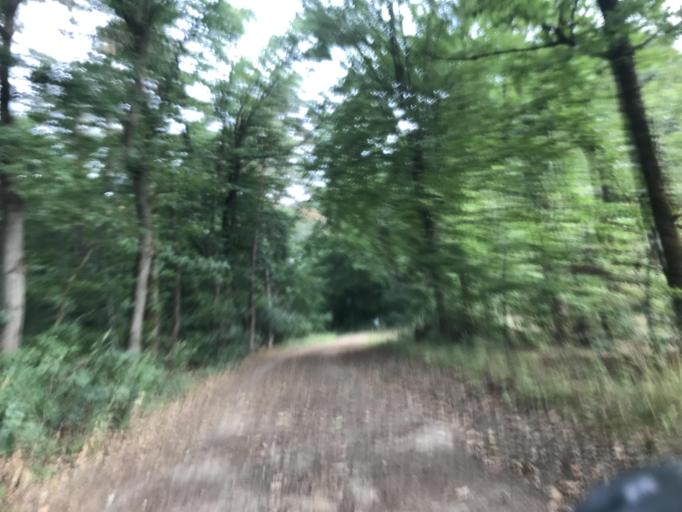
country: DE
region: Lower Saxony
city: Vastorf
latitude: 53.2132
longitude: 10.5405
